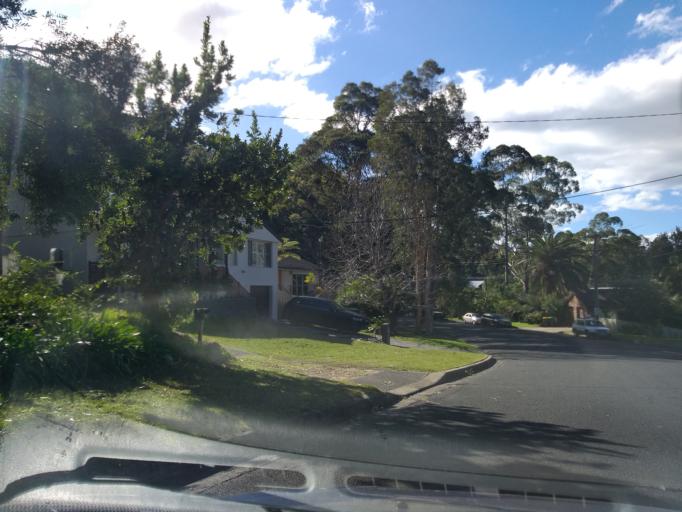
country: AU
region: New South Wales
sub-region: Wollongong
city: Bulli
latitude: -34.3051
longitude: 150.9233
